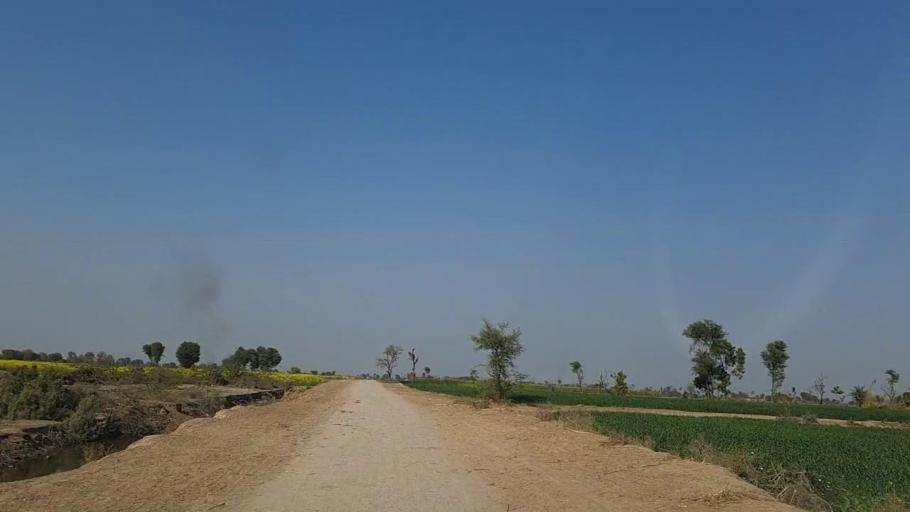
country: PK
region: Sindh
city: Daur
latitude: 26.4392
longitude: 68.2628
